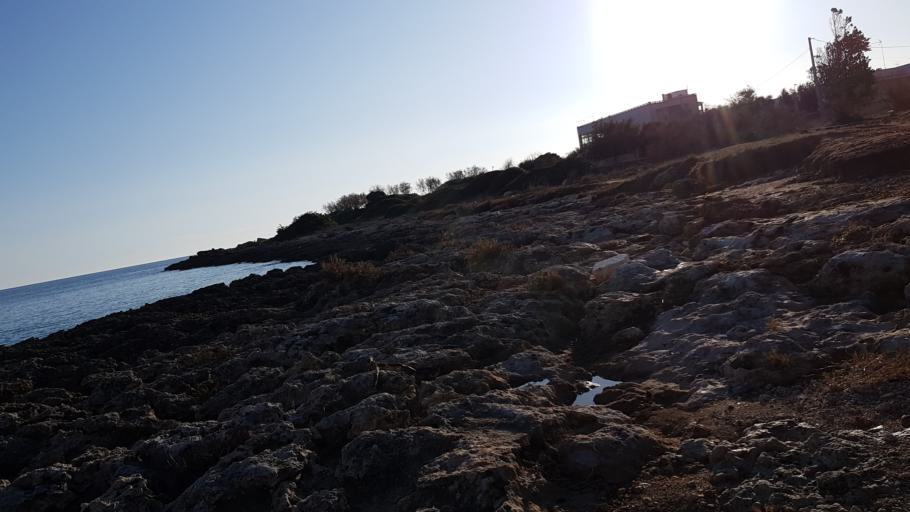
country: IT
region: Apulia
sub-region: Provincia di Taranto
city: Avetrana
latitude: 40.2937
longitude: 17.7668
